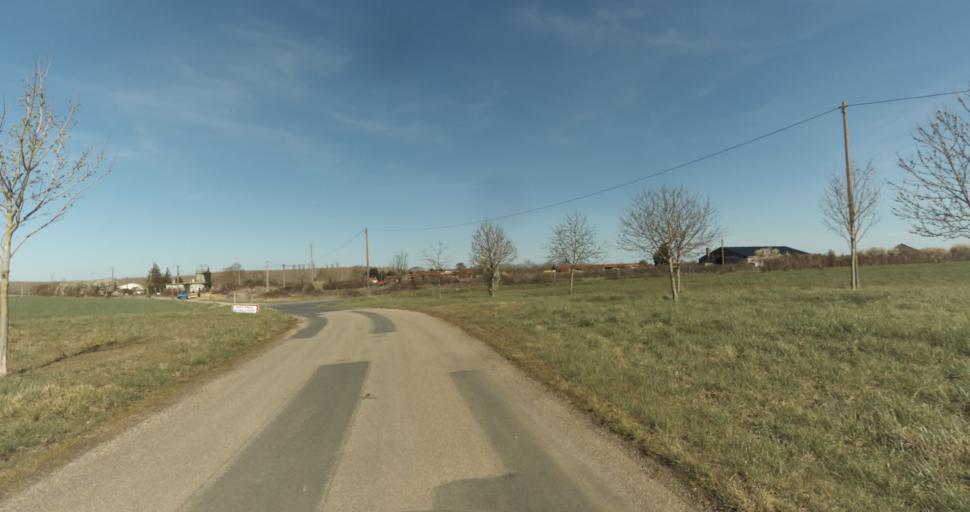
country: FR
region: Lower Normandy
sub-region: Departement du Calvados
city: Saint-Pierre-sur-Dives
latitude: 49.0501
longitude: -0.0541
